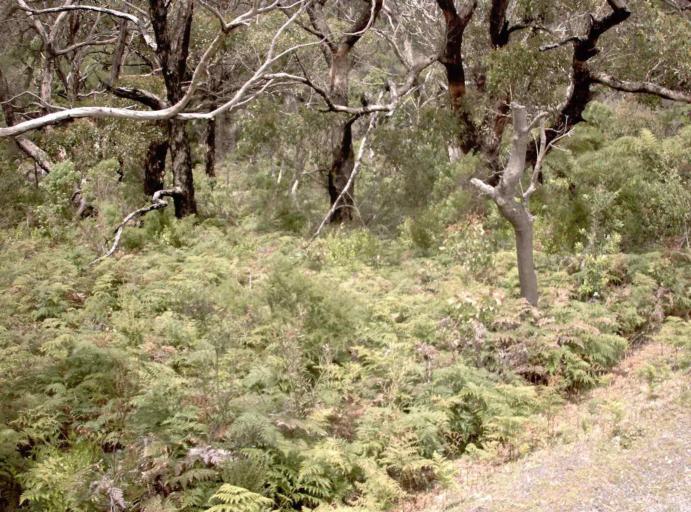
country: AU
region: Victoria
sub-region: Latrobe
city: Morwell
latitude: -39.0113
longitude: 146.2982
